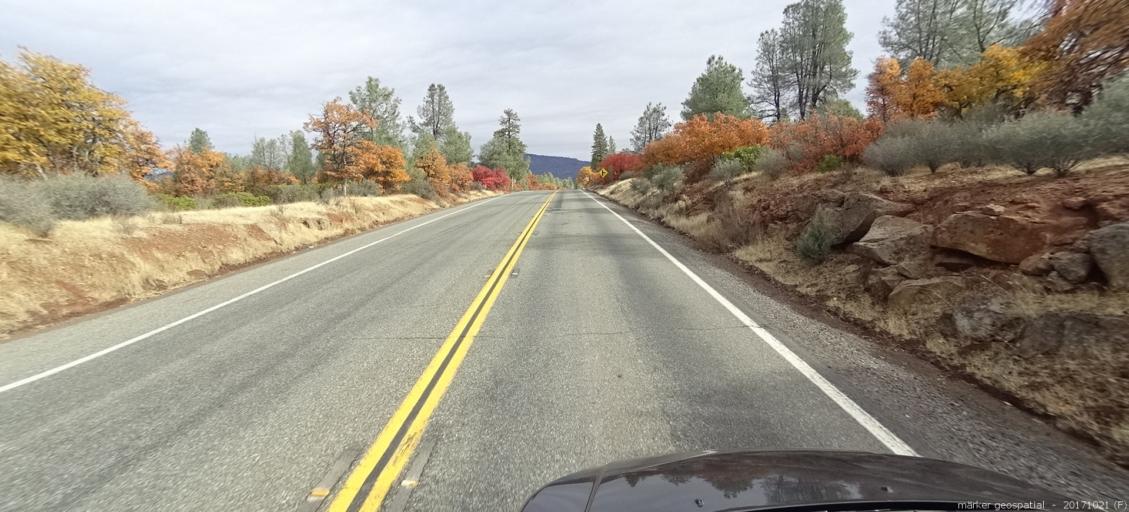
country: US
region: California
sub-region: Shasta County
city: Burney
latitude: 40.9658
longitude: -121.5745
